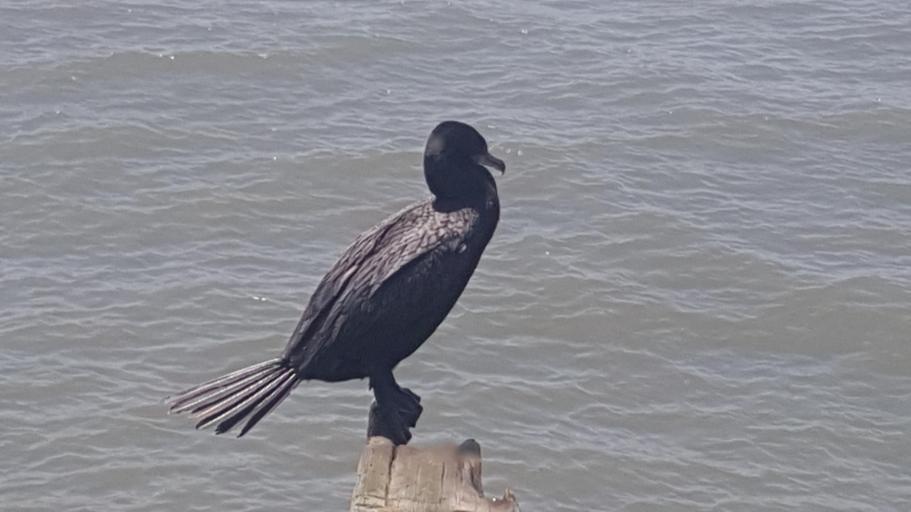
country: PE
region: Lambayeque
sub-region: Provincia de Chiclayo
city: Pimentel
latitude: -6.8394
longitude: -79.9378
